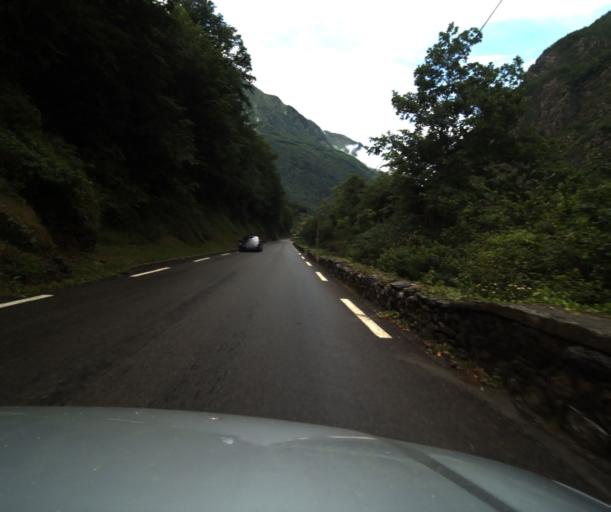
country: FR
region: Midi-Pyrenees
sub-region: Departement des Hautes-Pyrenees
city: Luz-Saint-Sauveur
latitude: 42.8309
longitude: 0.0040
